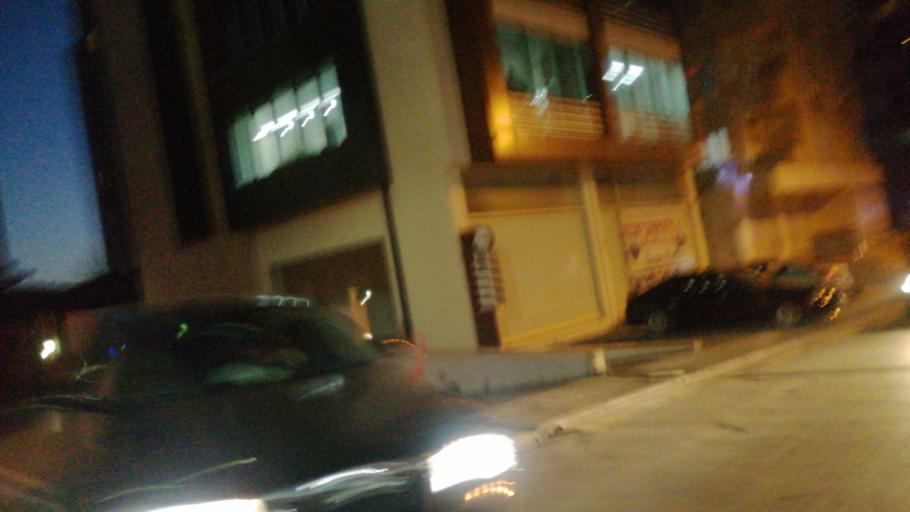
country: TR
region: Istanbul
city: Umraniye
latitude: 40.9987
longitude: 29.1423
